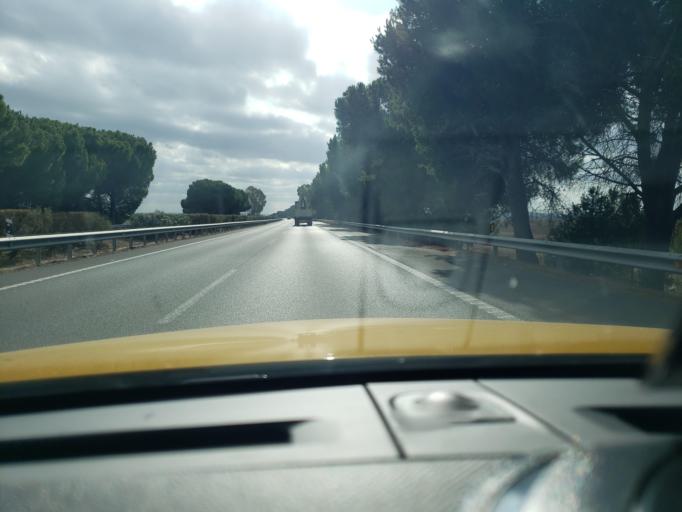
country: ES
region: Andalusia
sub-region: Provincia de Sevilla
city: Las Cabezas de San Juan
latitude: 37.0643
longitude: -5.9347
